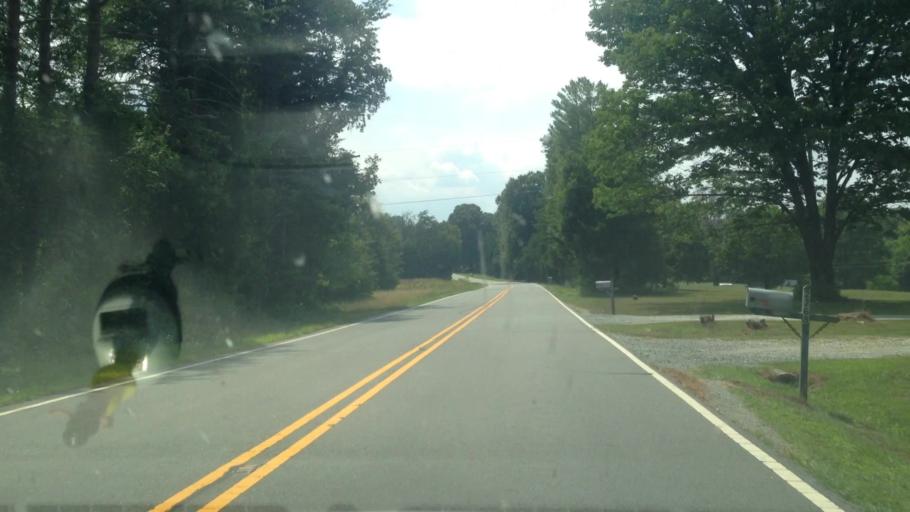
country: US
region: North Carolina
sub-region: Stokes County
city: Walnut Cove
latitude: 36.3718
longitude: -80.0725
